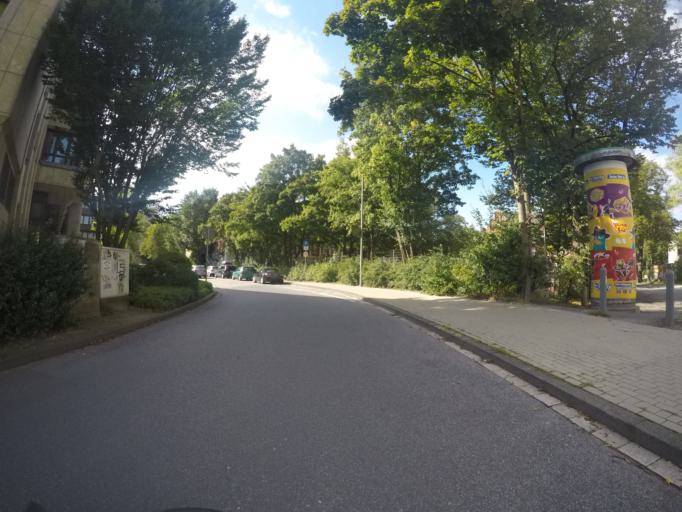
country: DE
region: North Rhine-Westphalia
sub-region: Regierungsbezirk Detmold
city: Herford
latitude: 52.1174
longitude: 8.6722
